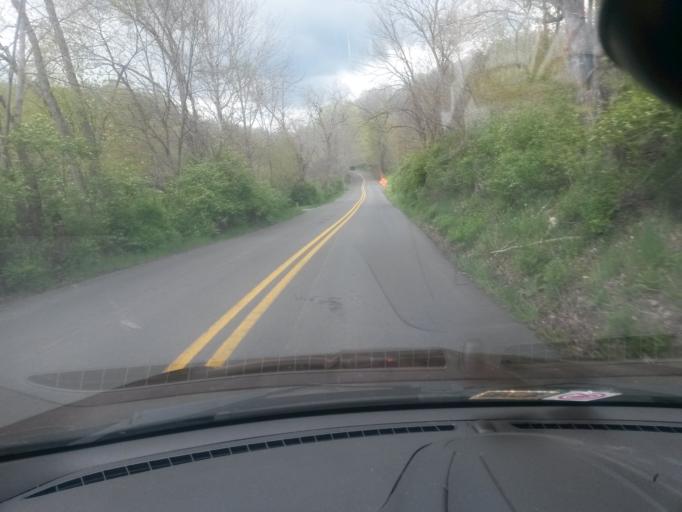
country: US
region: West Virginia
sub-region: Greenbrier County
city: Lewisburg
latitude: 37.9342
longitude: -80.4058
